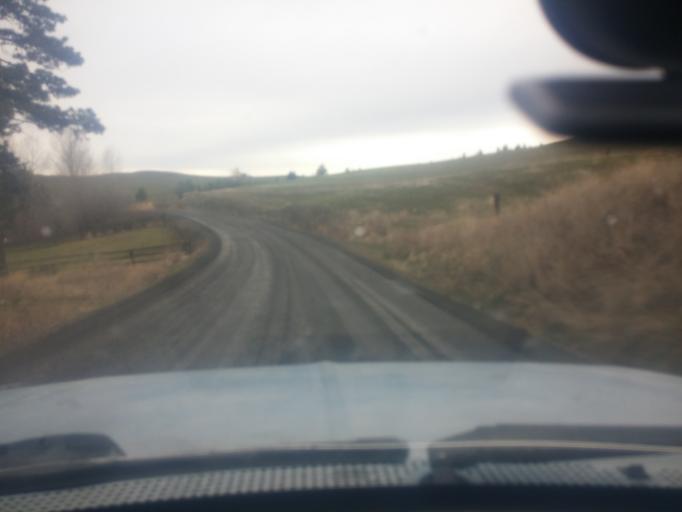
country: US
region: Idaho
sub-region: Latah County
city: Moscow
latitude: 46.9255
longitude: -116.8621
